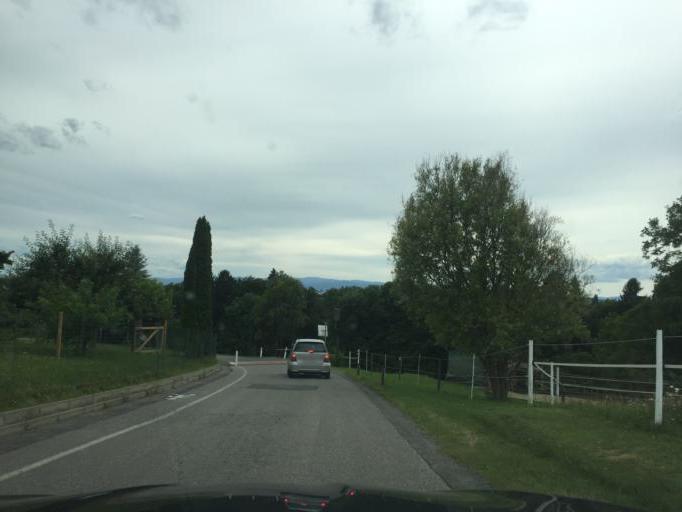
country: AT
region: Styria
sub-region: Politischer Bezirk Graz-Umgebung
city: Hart bei Graz
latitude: 47.0597
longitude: 15.5142
